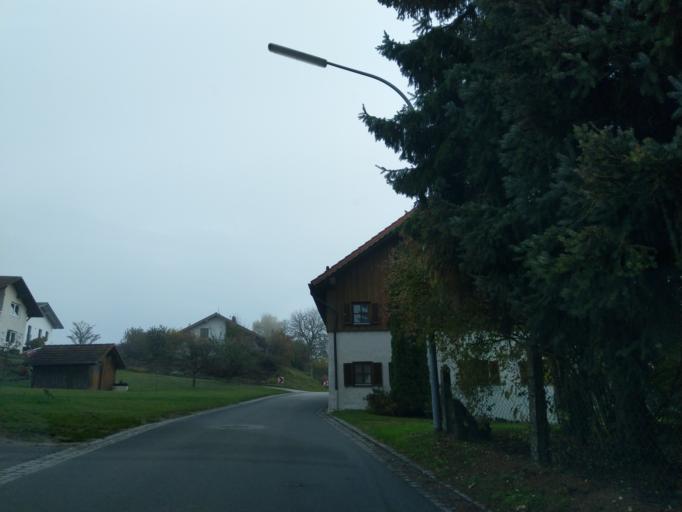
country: DE
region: Bavaria
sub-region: Lower Bavaria
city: Grattersdorf
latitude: 48.7949
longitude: 13.1559
